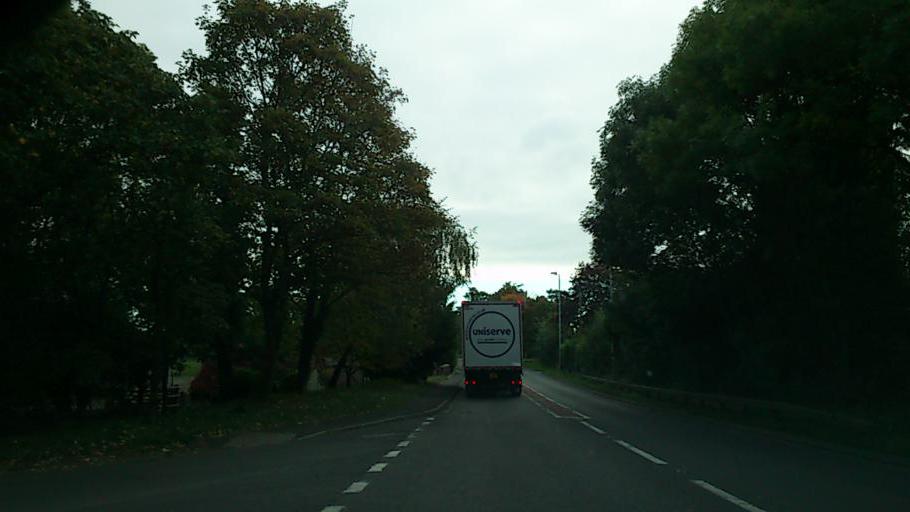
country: GB
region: England
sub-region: Shropshire
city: Ford
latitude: 52.7133
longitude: -2.8704
